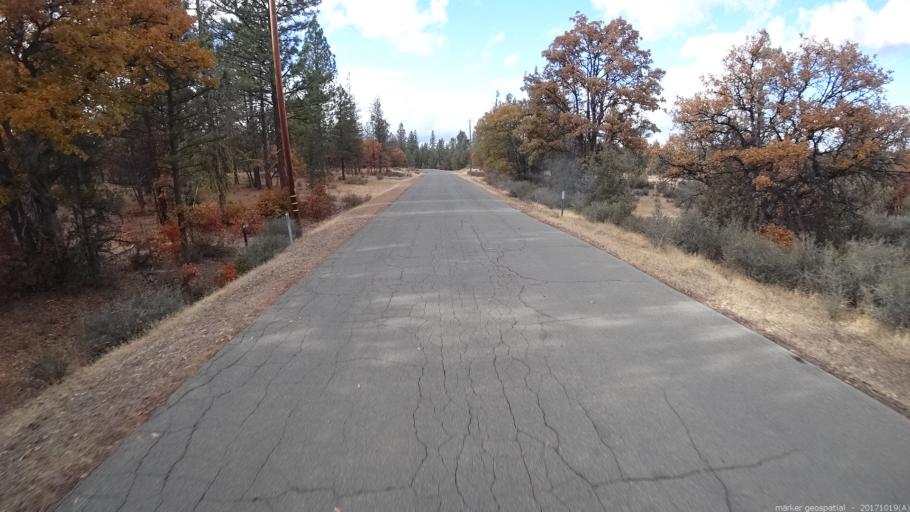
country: US
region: California
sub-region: Shasta County
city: Burney
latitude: 40.9718
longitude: -121.4366
